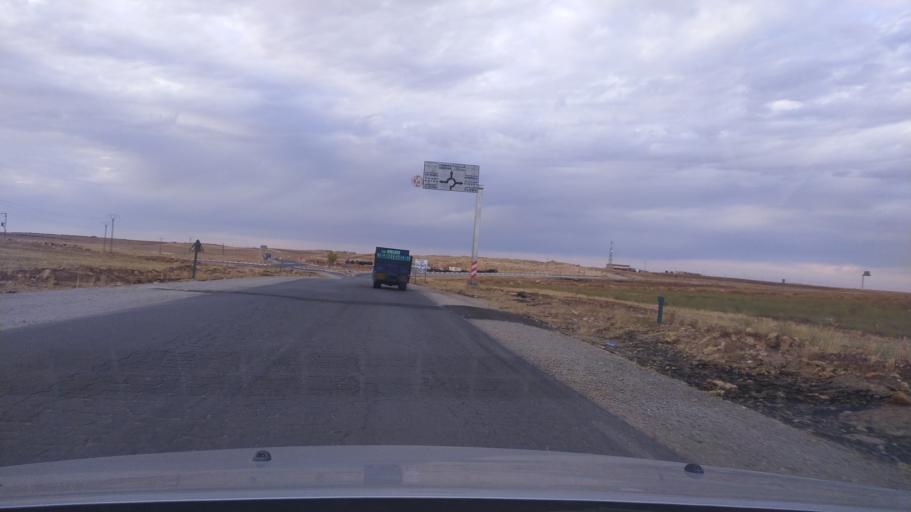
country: DZ
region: Tiaret
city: Frenda
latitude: 34.9898
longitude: 1.1310
